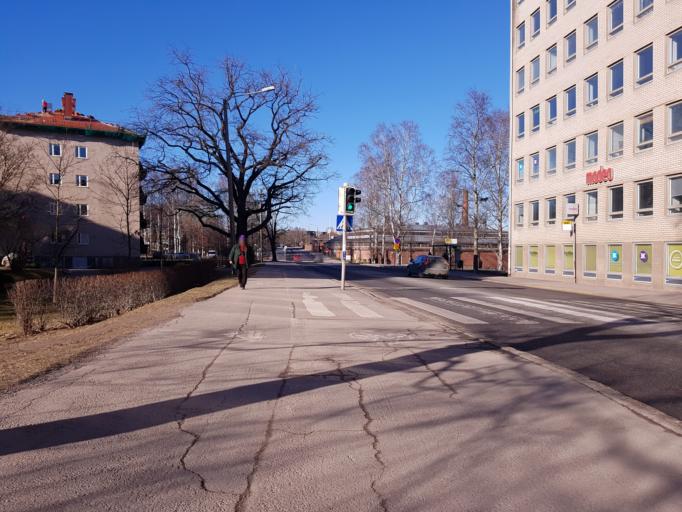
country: FI
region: Uusimaa
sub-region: Helsinki
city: Helsinki
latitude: 60.2127
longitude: 24.9782
